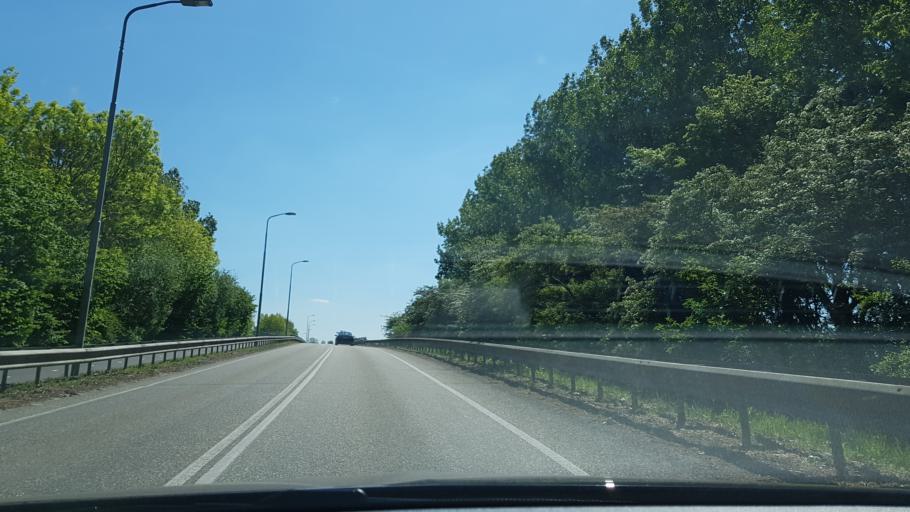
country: NL
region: North Holland
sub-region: Gemeente Haarlemmermeer
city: Hoofddorp
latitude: 52.2680
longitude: 4.6946
